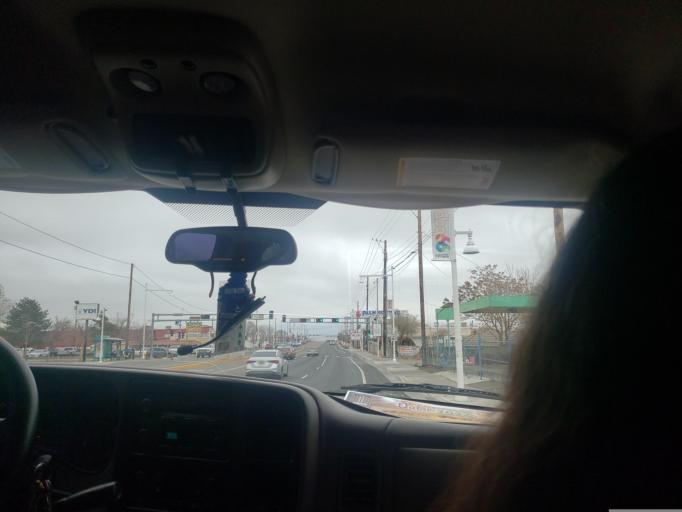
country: US
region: New Mexico
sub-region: Bernalillo County
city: Albuquerque
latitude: 35.0805
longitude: -106.7079
